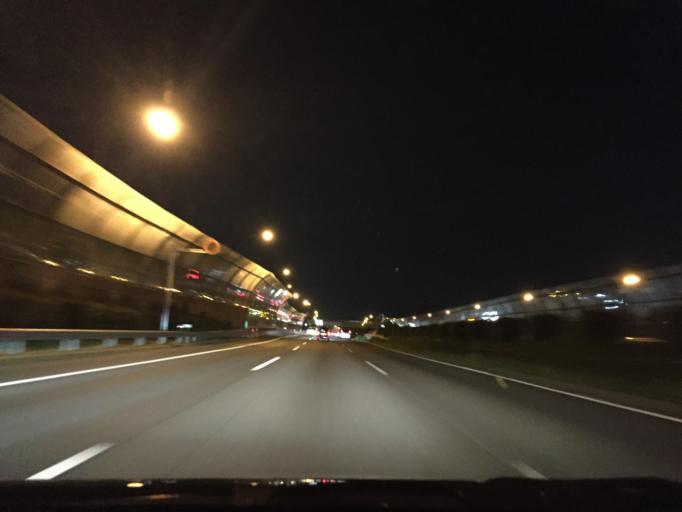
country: JP
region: Kanagawa
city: Atsugi
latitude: 35.4373
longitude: 139.4048
